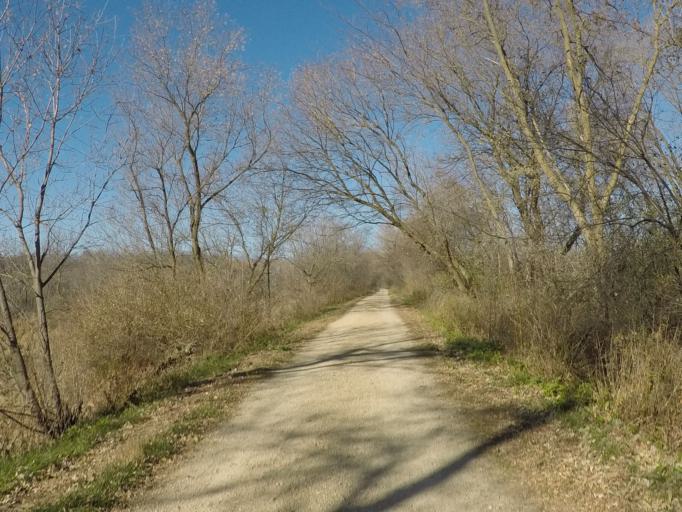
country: US
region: Wisconsin
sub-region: Dane County
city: Deerfield
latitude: 43.0497
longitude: -89.0616
